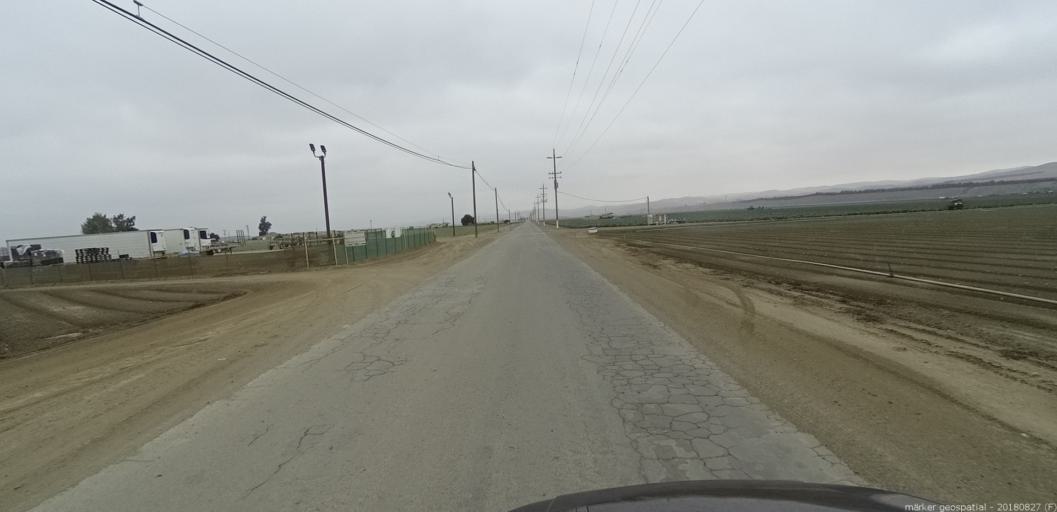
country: US
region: California
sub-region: Monterey County
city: King City
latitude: 36.2462
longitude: -121.1478
